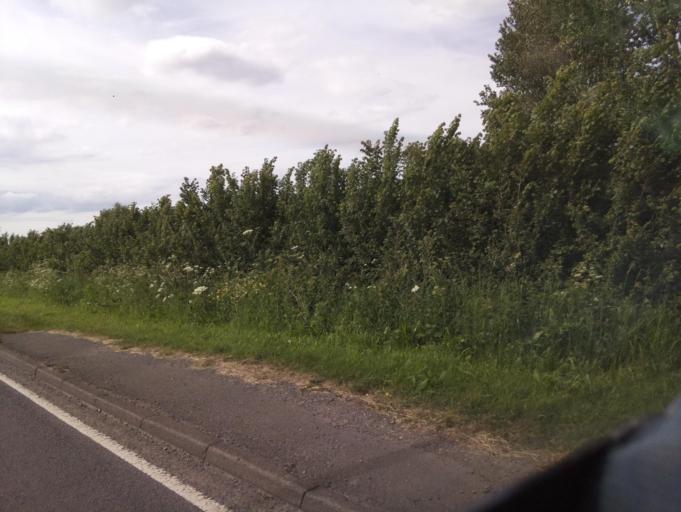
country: GB
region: England
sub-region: Worcestershire
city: Pershore
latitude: 52.0991
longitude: -2.0170
